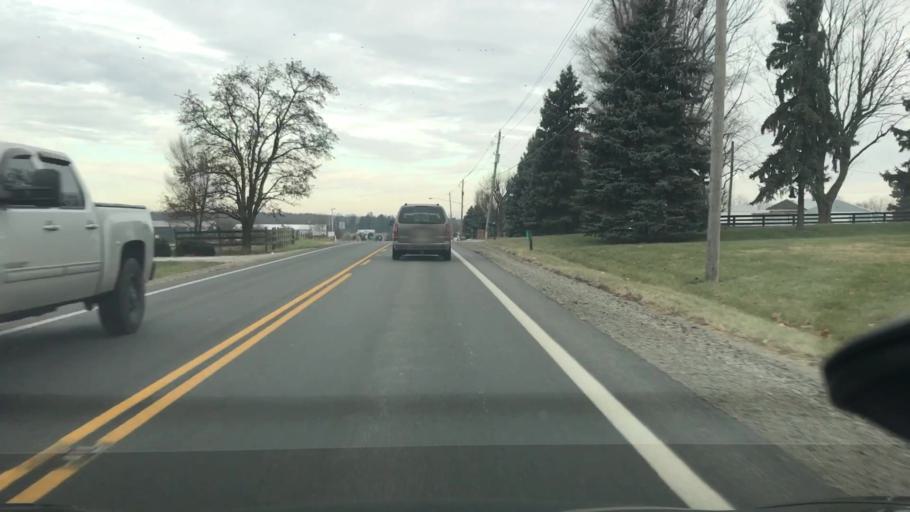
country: US
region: Ohio
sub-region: Madison County
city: Choctaw Lake
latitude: 39.9374
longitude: -83.4944
